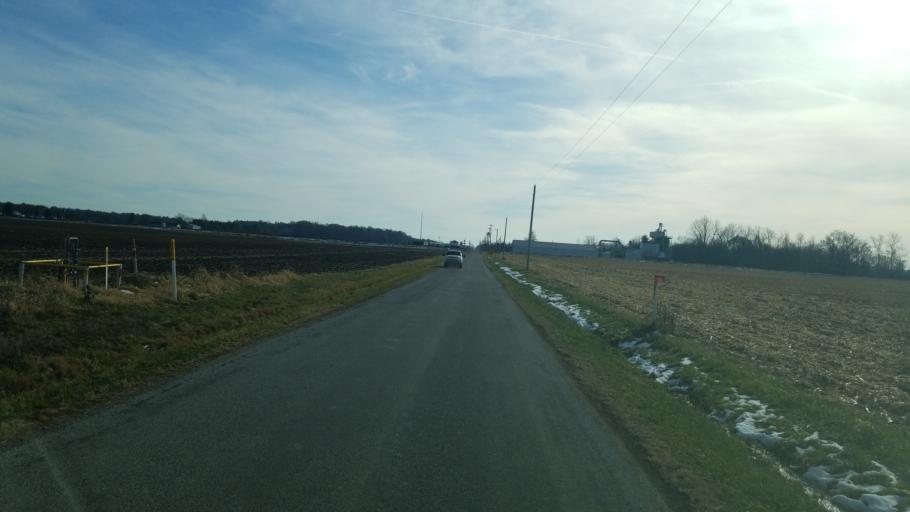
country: US
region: Ohio
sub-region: Huron County
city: New London
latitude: 41.0360
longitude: -82.2802
